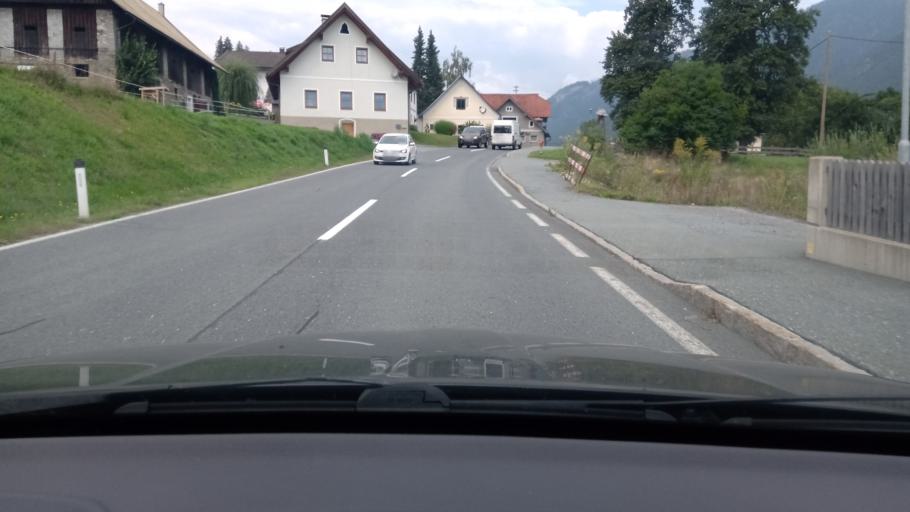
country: AT
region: Carinthia
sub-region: Politischer Bezirk Hermagor
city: Hermagor
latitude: 46.6360
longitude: 13.3481
